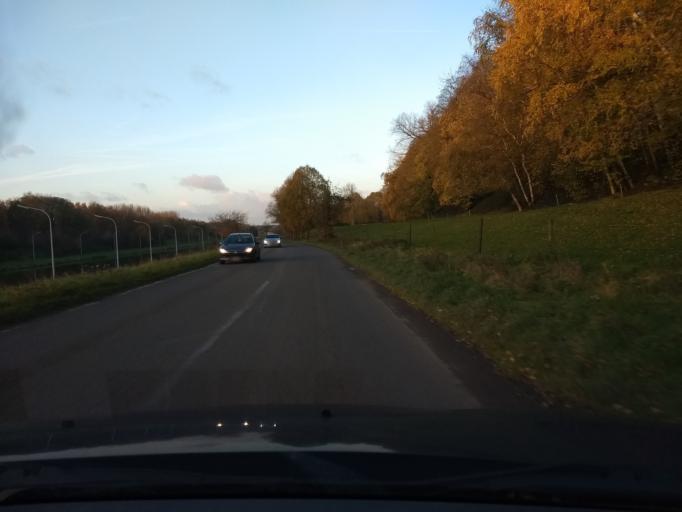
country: BE
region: Wallonia
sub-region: Province du Brabant Wallon
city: Ittre
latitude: 50.6094
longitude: 4.2255
